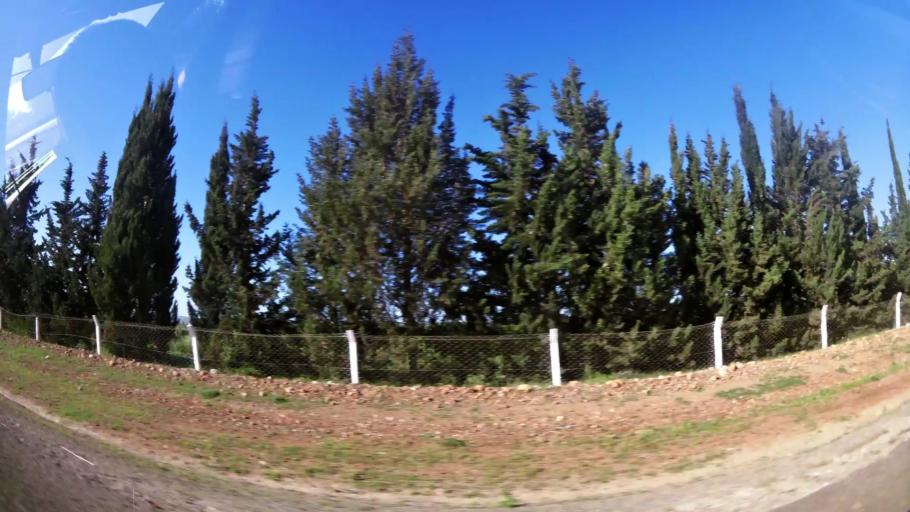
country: MA
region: Oriental
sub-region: Berkane-Taourirt
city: Ahfir
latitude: 35.0009
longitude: -2.1761
